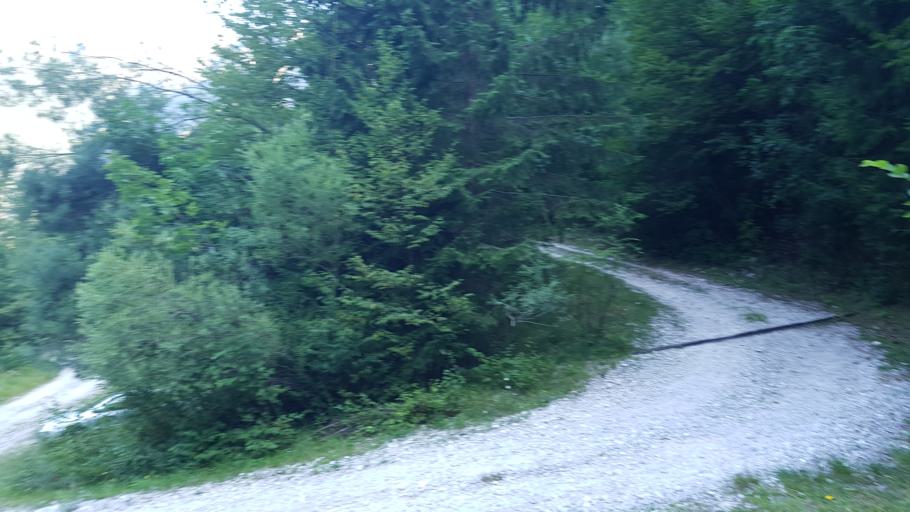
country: SI
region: Kranjska Gora
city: Kranjska Gora
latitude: 46.3695
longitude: 13.7475
